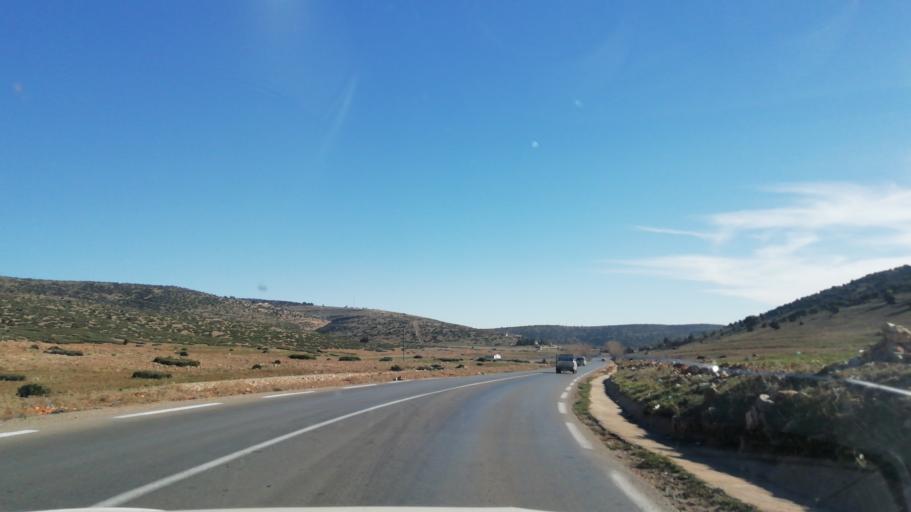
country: DZ
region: Tlemcen
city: Sebdou
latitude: 34.7141
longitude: -1.3261
